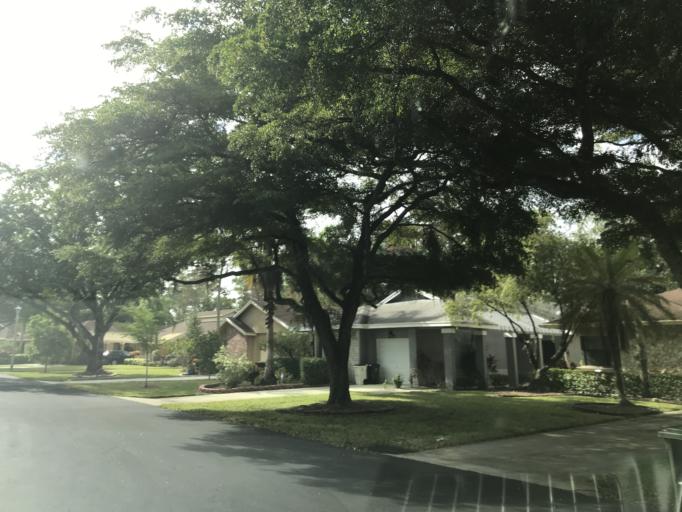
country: US
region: Florida
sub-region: Broward County
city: Coconut Creek
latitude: 26.2626
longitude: -80.1906
